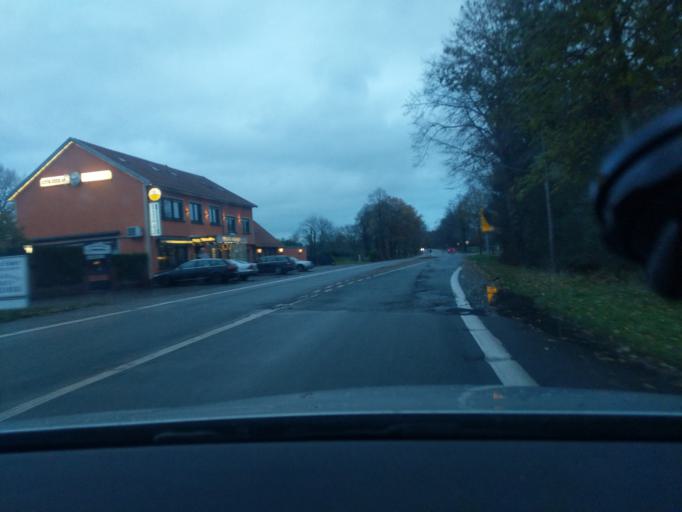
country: DE
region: North Rhine-Westphalia
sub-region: Regierungsbezirk Arnsberg
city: Hamm
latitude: 51.6979
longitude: 7.8814
